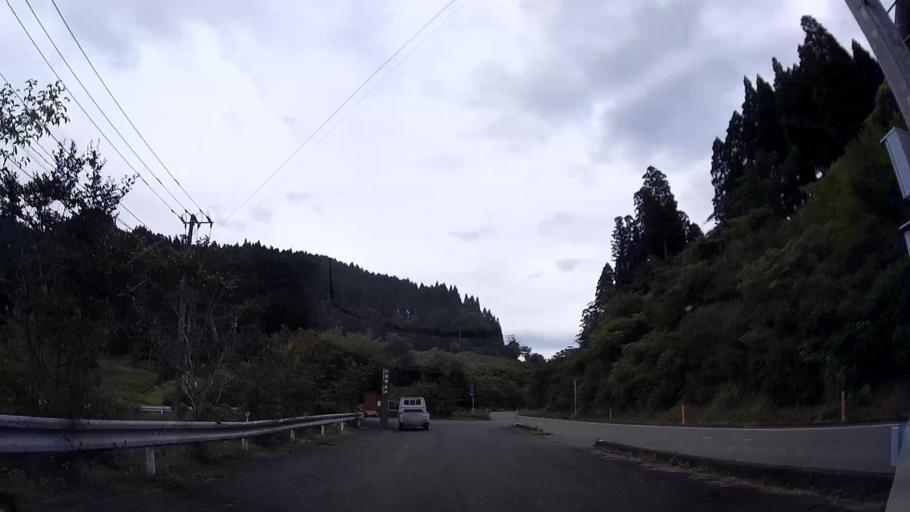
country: JP
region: Oita
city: Hita
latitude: 33.1371
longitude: 130.9852
